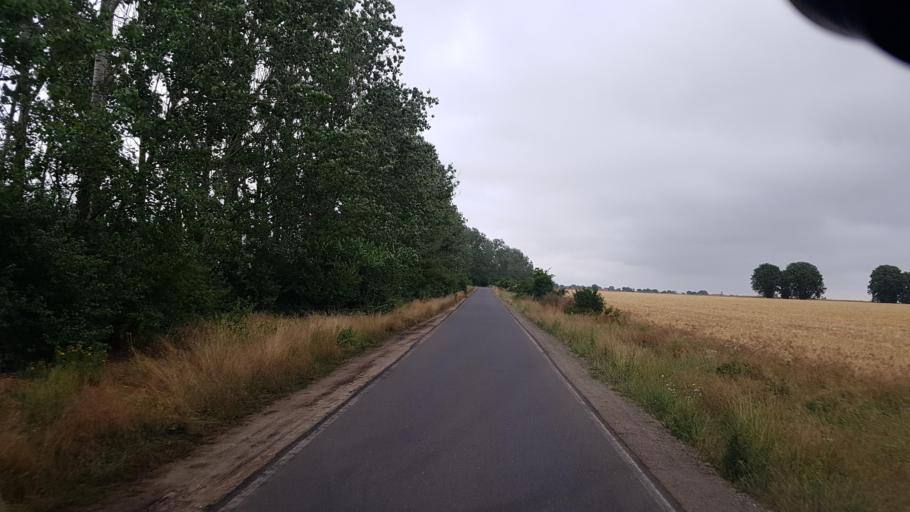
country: DE
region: Brandenburg
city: Ihlow
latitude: 51.9111
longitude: 13.2007
